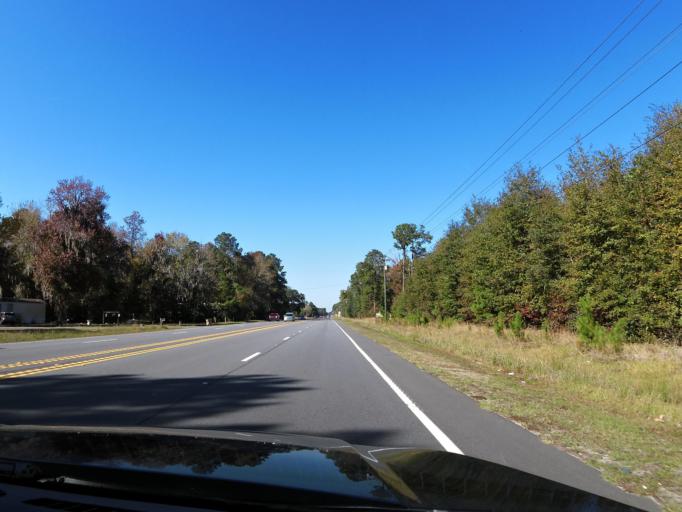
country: US
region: Georgia
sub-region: Liberty County
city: Midway
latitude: 31.7850
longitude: -81.3897
